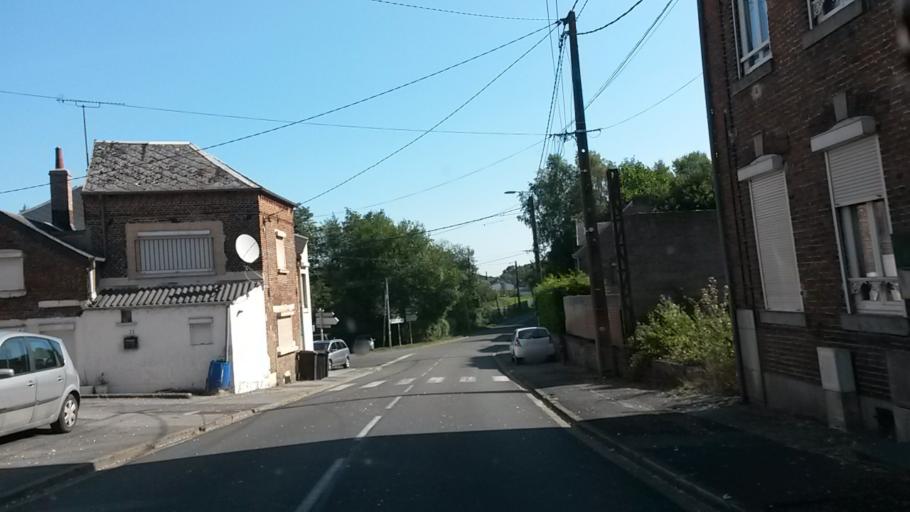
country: FR
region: Nord-Pas-de-Calais
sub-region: Departement du Nord
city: Avesnelles
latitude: 50.1205
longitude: 3.9506
